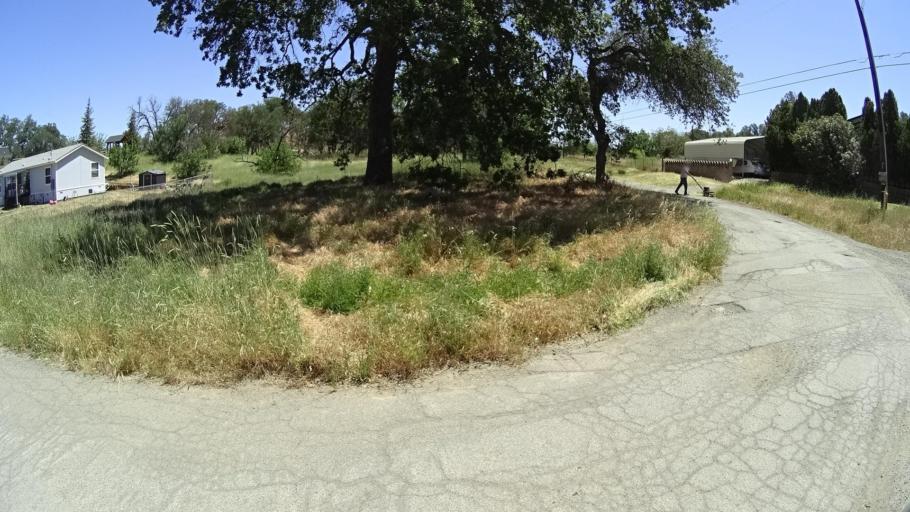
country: US
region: California
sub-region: Lake County
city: Lower Lake
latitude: 38.9088
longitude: -122.6060
